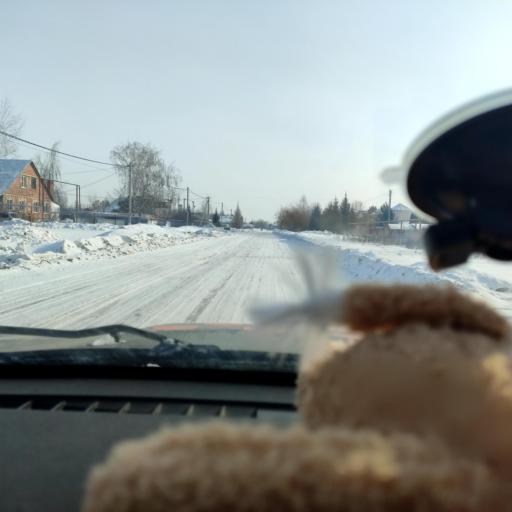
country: RU
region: Samara
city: Podstepki
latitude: 53.5107
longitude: 49.1220
